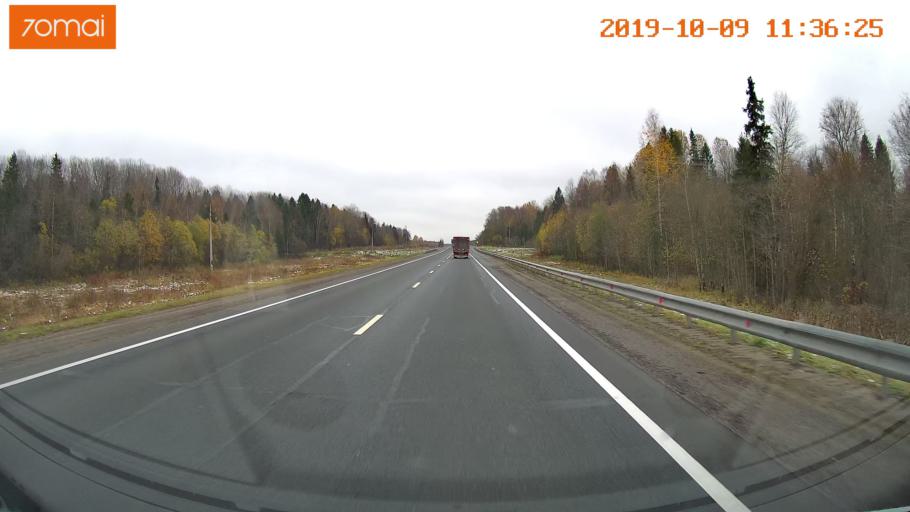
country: RU
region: Vologda
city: Gryazovets
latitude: 58.9909
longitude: 40.1366
